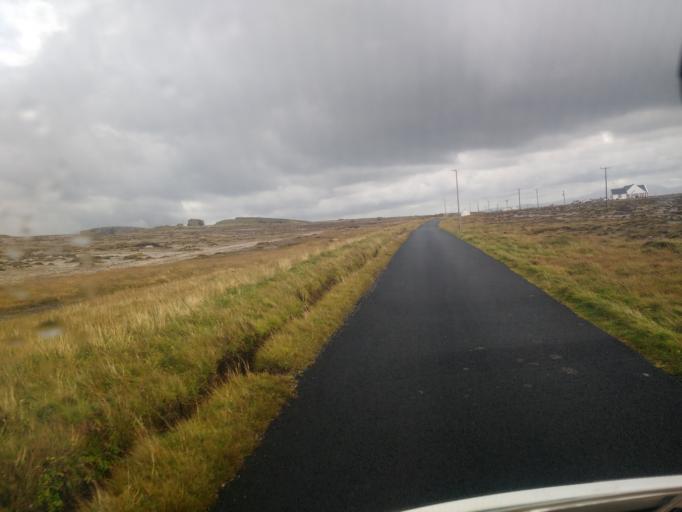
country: IE
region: Ulster
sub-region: County Donegal
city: Derrybeg
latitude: 55.2625
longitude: -8.2162
